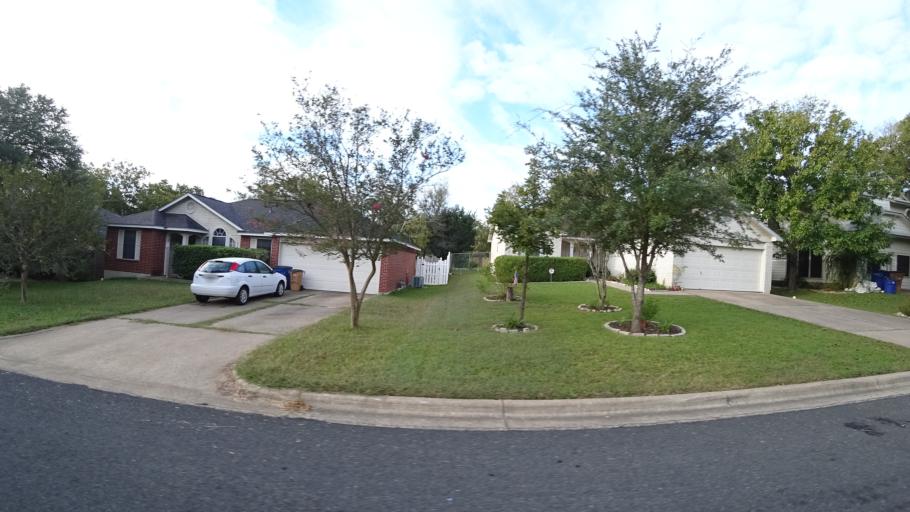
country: US
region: Texas
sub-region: Travis County
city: Onion Creek
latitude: 30.1922
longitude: -97.7356
